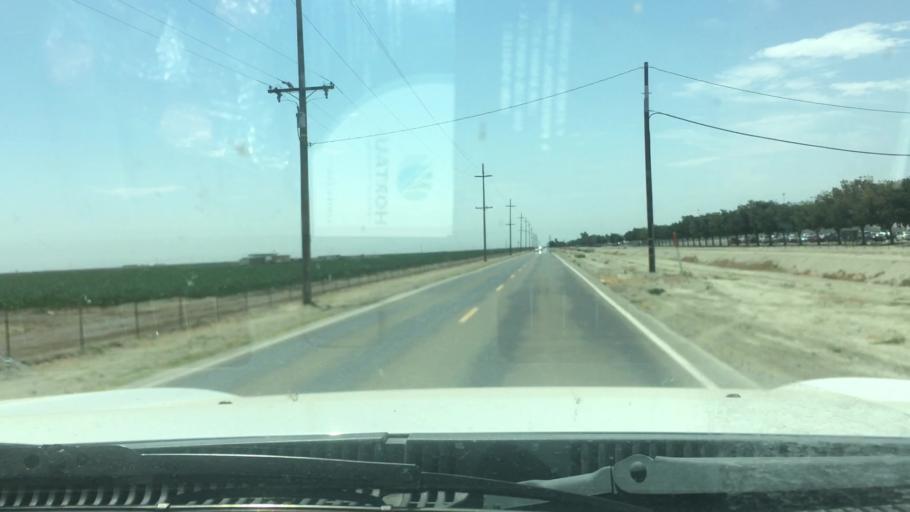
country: US
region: California
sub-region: Kings County
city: Corcoran
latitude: 36.0508
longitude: -119.5420
